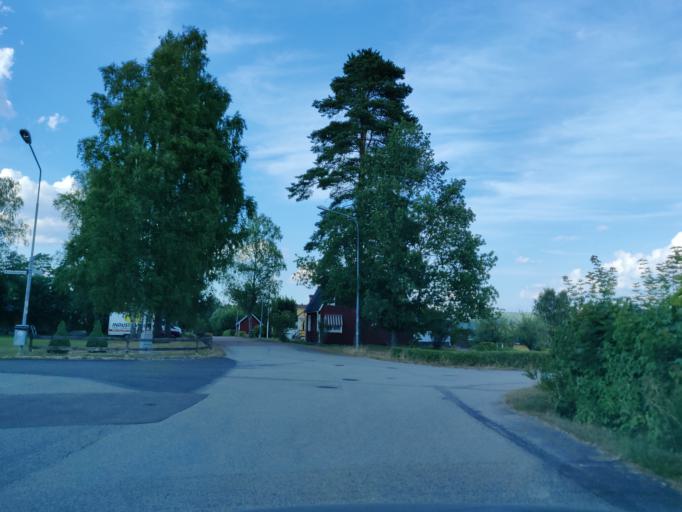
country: SE
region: Vaermland
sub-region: Hagfors Kommun
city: Hagfors
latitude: 60.0182
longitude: 13.6795
